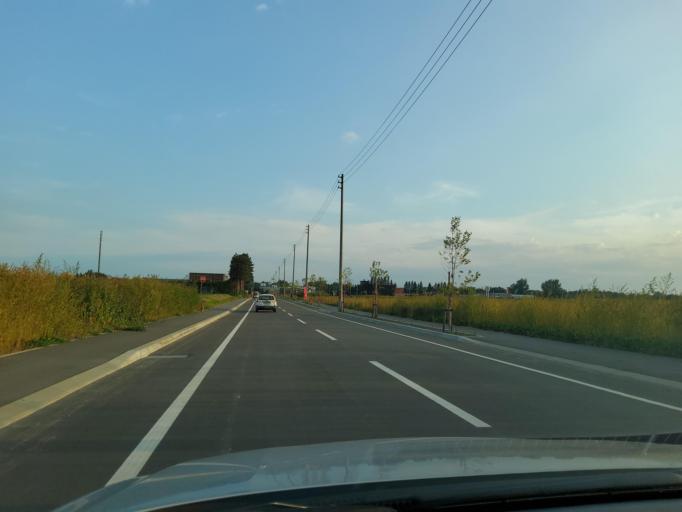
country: JP
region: Hokkaido
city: Obihiro
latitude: 42.9375
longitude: 143.1531
